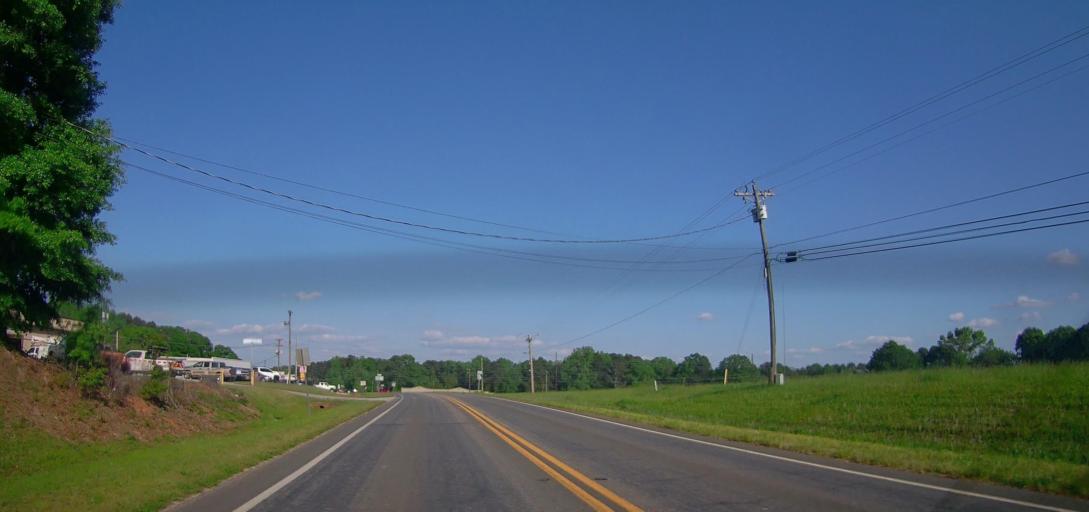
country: US
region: Georgia
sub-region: Morgan County
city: Madison
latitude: 33.5816
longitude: -83.4922
